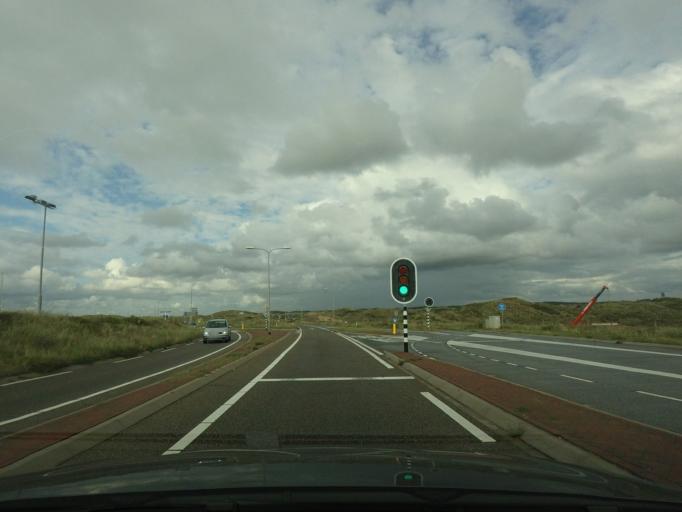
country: NL
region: North Holland
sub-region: Gemeente Zandvoort
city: Zandvoort
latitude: 52.4016
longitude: 4.5452
